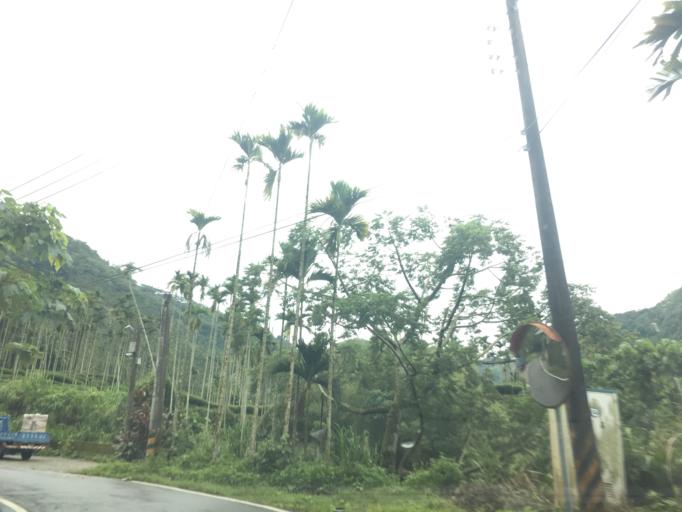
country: TW
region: Taiwan
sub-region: Yunlin
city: Douliu
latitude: 23.5620
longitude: 120.6473
